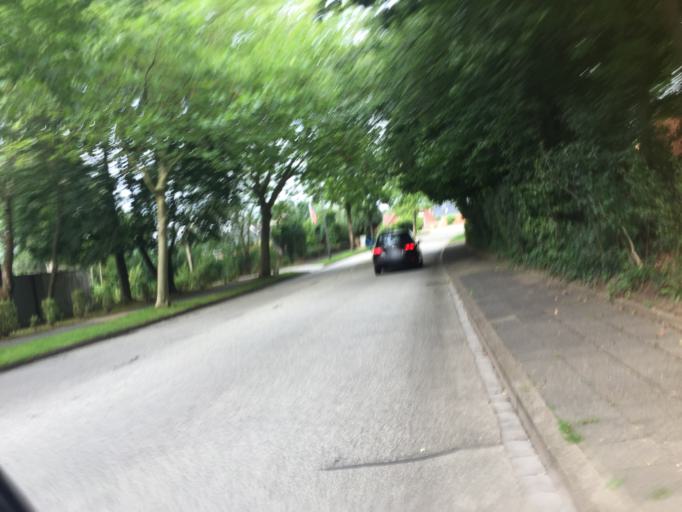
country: DE
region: Schleswig-Holstein
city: Ottenbuttel
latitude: 53.9483
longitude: 9.5045
